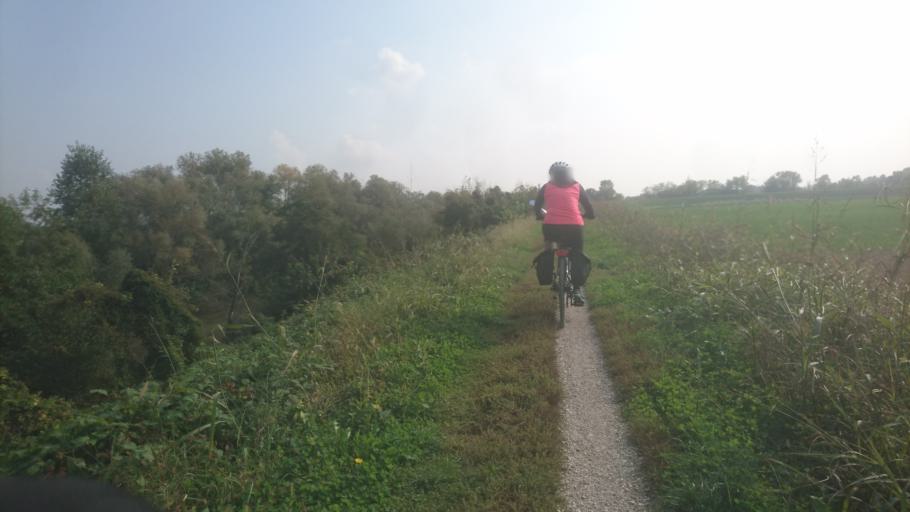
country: IT
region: Veneto
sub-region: Provincia di Vicenza
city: Quinto Vicentino
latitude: 45.5692
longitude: 11.6270
